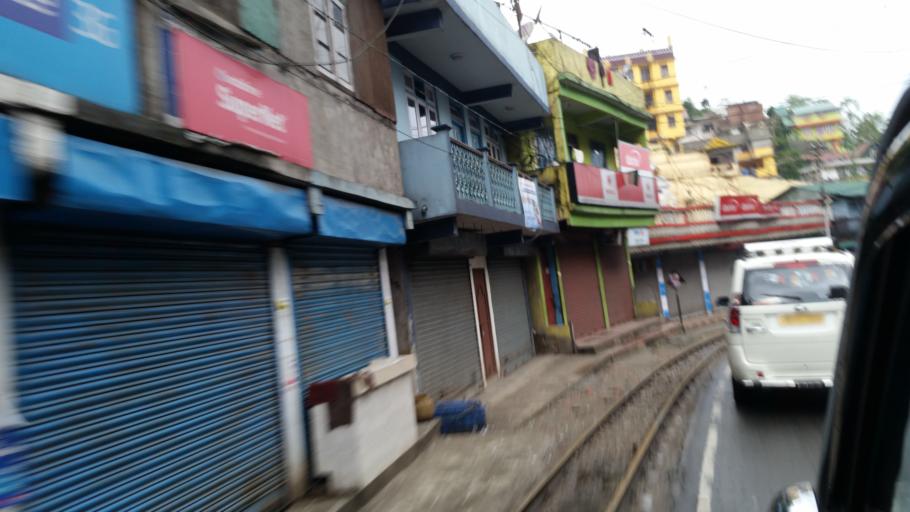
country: IN
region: West Bengal
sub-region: Darjiling
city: Darjiling
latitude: 27.0085
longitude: 88.2522
